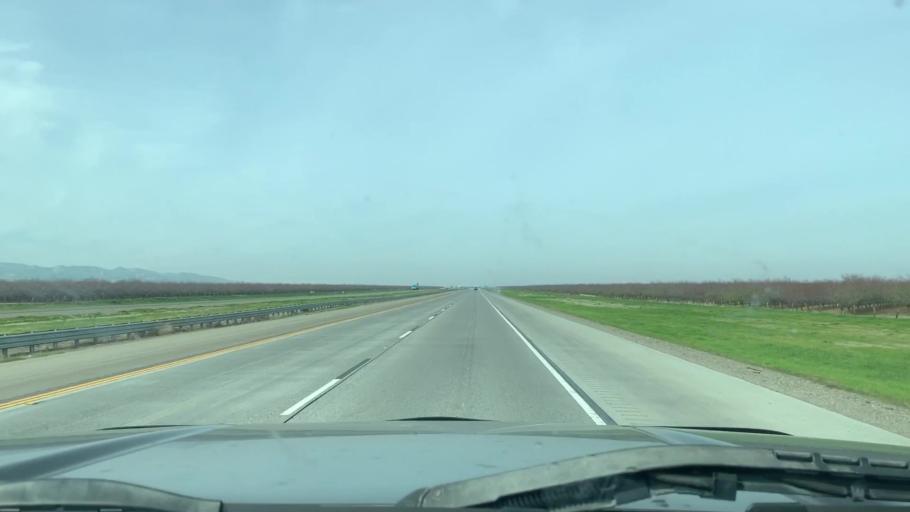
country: US
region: California
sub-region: Fresno County
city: Firebaugh
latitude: 36.6625
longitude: -120.6402
